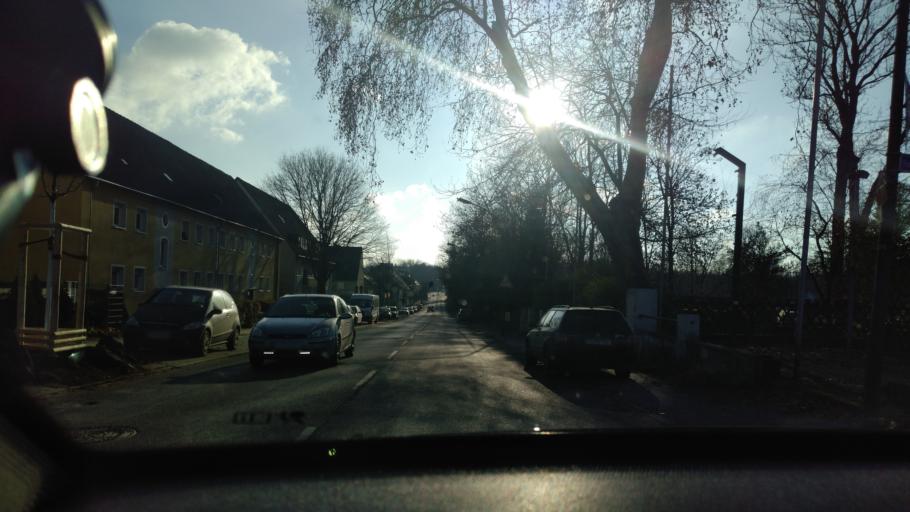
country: DE
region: North Rhine-Westphalia
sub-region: Regierungsbezirk Dusseldorf
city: Essen
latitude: 51.4931
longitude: 6.9804
